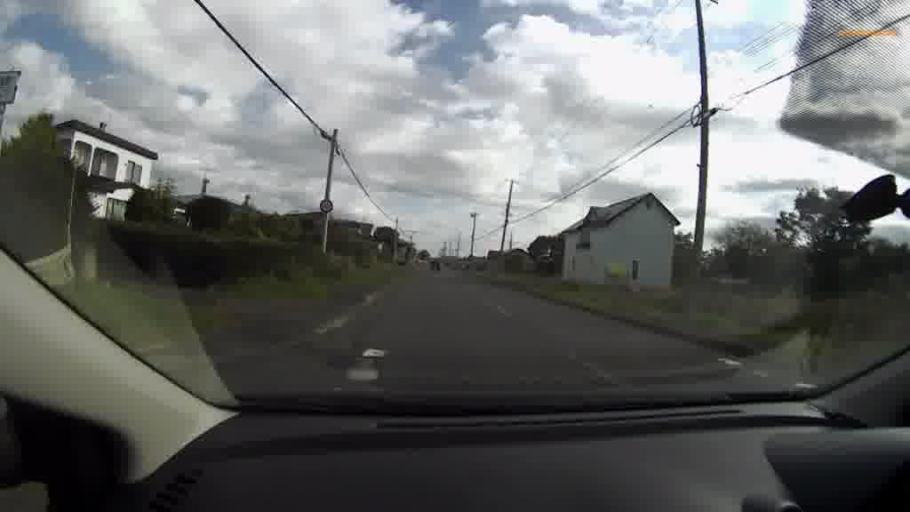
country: JP
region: Hokkaido
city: Kushiro
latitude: 42.9769
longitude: 144.1254
